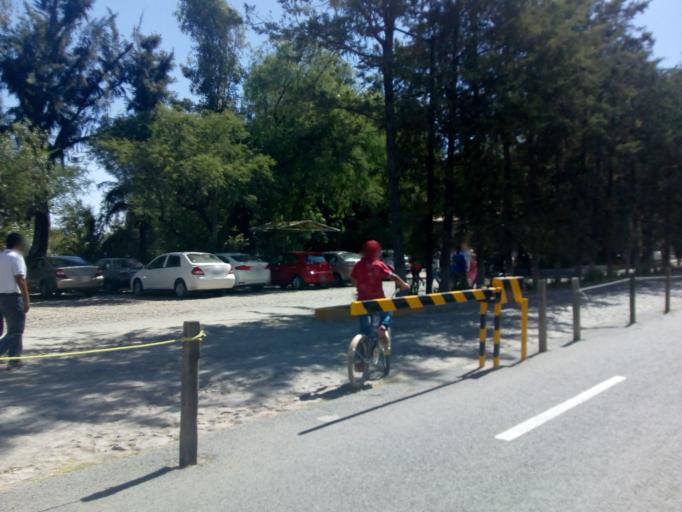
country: MX
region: Guanajuato
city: Leon
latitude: 21.1730
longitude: -101.6853
